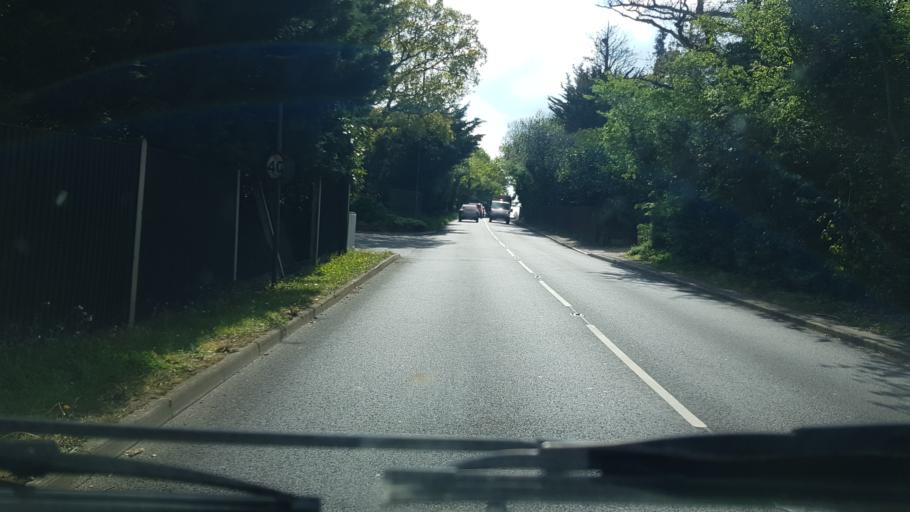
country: GB
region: England
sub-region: Surrey
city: Leatherhead
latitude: 51.3181
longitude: -0.3379
